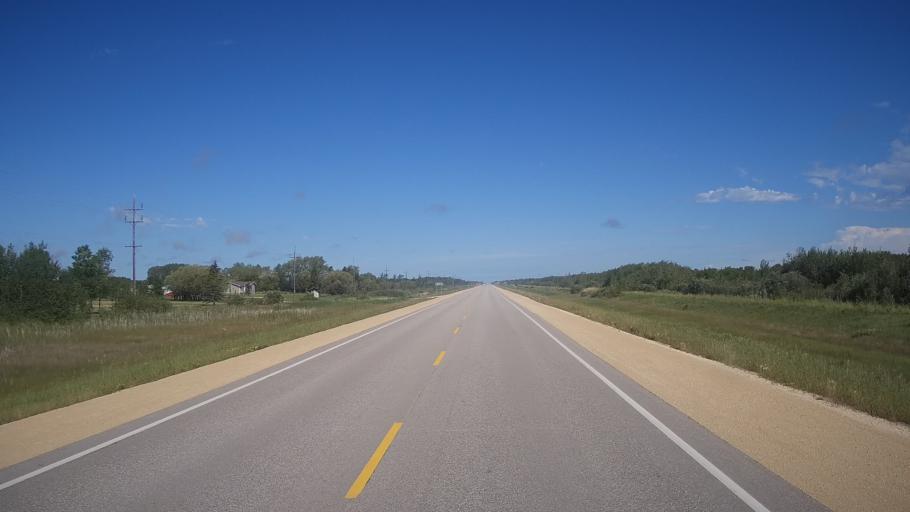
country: CA
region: Manitoba
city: Stonewall
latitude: 50.2347
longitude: -97.7049
